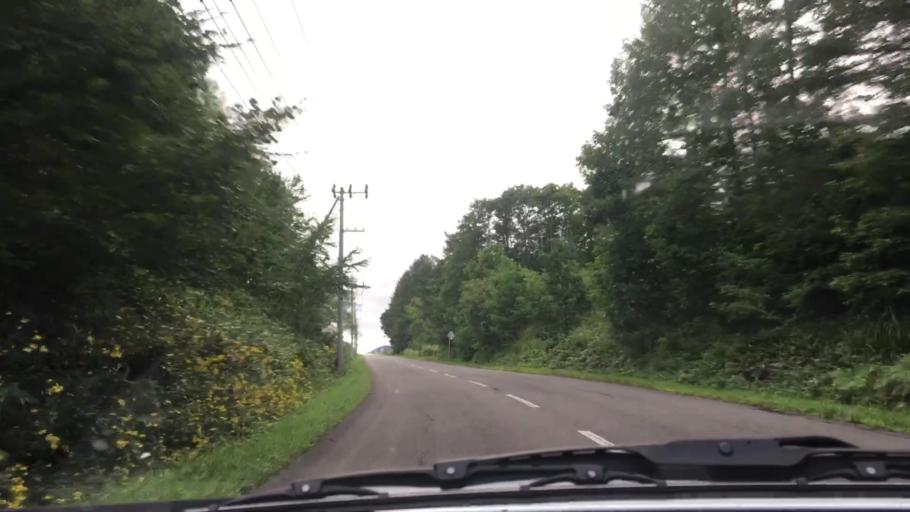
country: JP
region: Hokkaido
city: Otofuke
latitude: 43.1475
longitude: 142.8710
